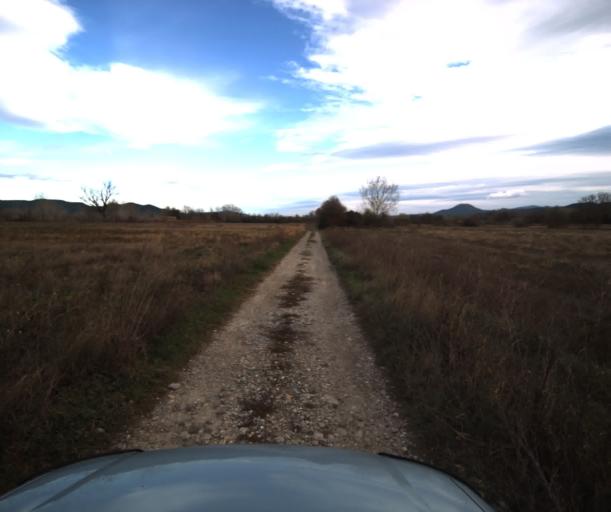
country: FR
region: Provence-Alpes-Cote d'Azur
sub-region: Departement du Vaucluse
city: Pertuis
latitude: 43.6672
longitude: 5.5168
